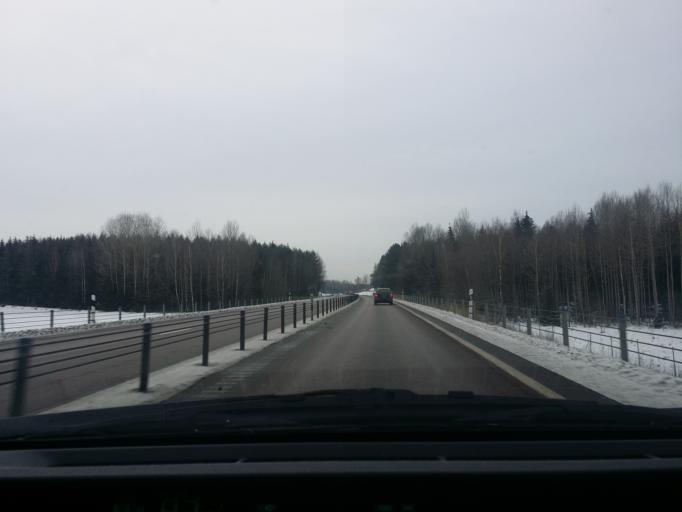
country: SE
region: Vaestra Goetaland
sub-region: Skovde Kommun
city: Stopen
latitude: 58.5379
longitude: 13.8128
